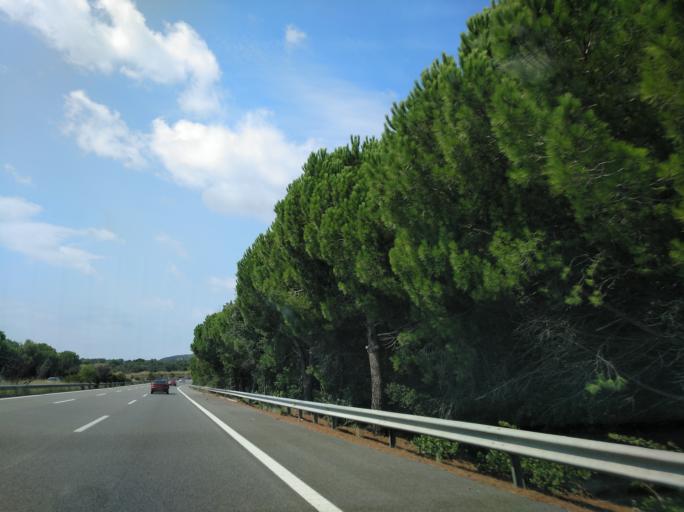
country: ES
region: Catalonia
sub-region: Provincia de Barcelona
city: Calella
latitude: 41.6308
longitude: 2.6672
